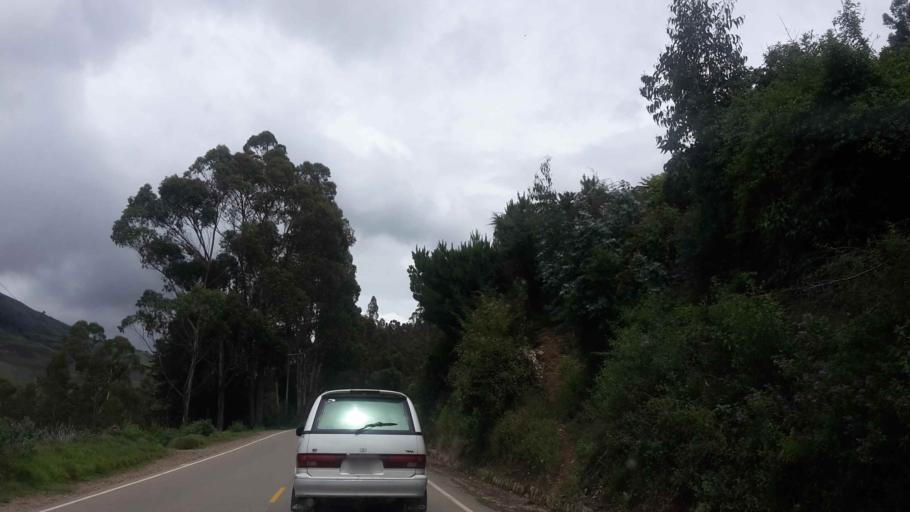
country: BO
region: Cochabamba
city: Totora
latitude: -17.5056
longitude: -65.4103
